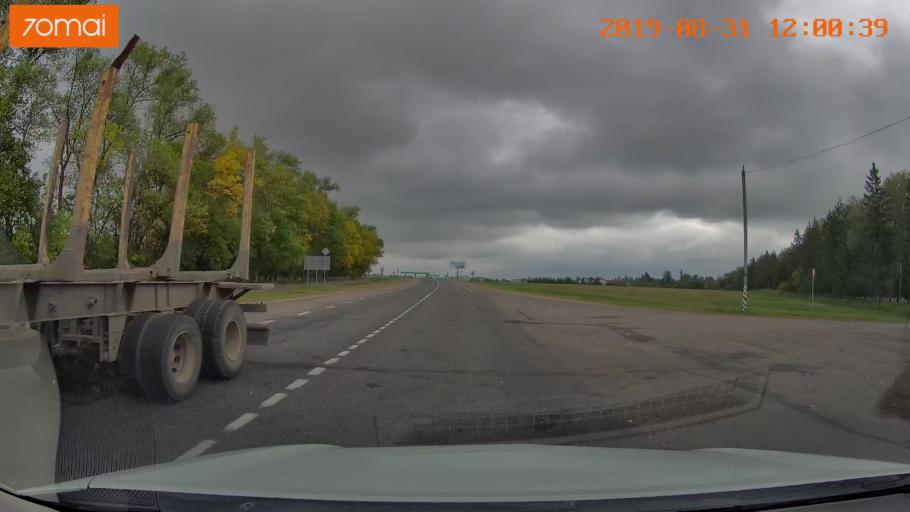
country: BY
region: Mogilev
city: Horad Krychaw
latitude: 53.6803
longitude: 31.6837
